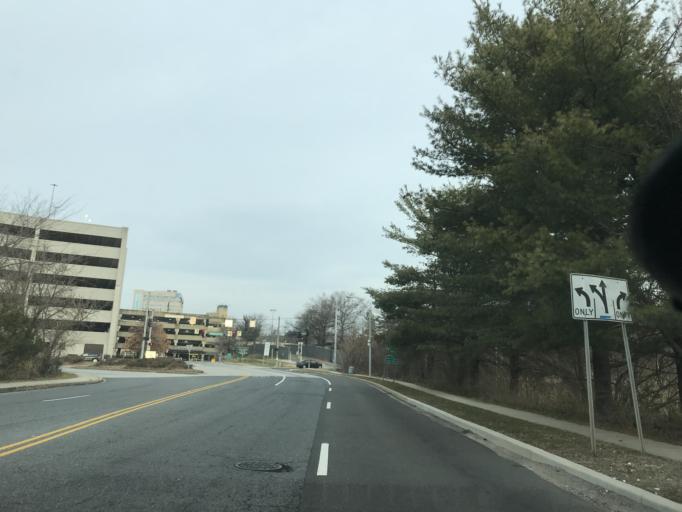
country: US
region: Maryland
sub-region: Prince George's County
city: Glenarden
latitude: 38.9474
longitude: -76.8684
